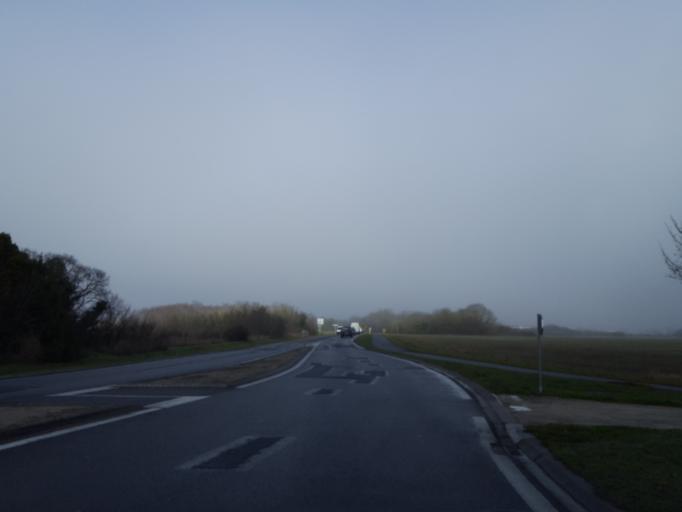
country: FR
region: Poitou-Charentes
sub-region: Departement de la Charente-Maritime
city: La Flotte
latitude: 46.1943
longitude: -1.3471
